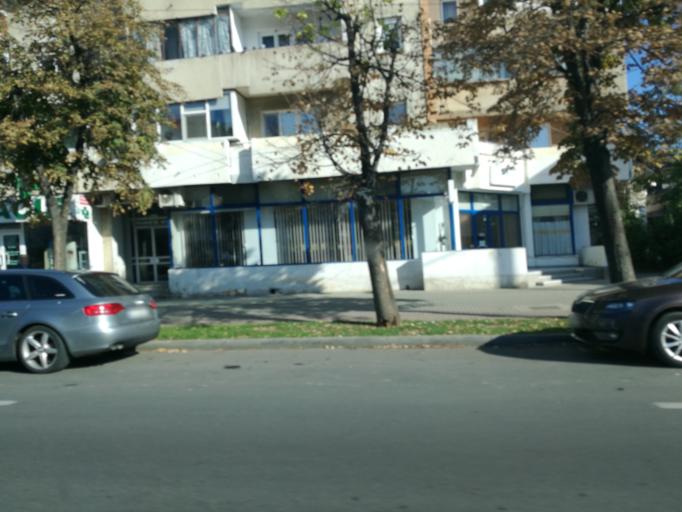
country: RO
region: Iasi
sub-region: Municipiul Iasi
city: Iasi
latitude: 47.1736
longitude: 27.5593
